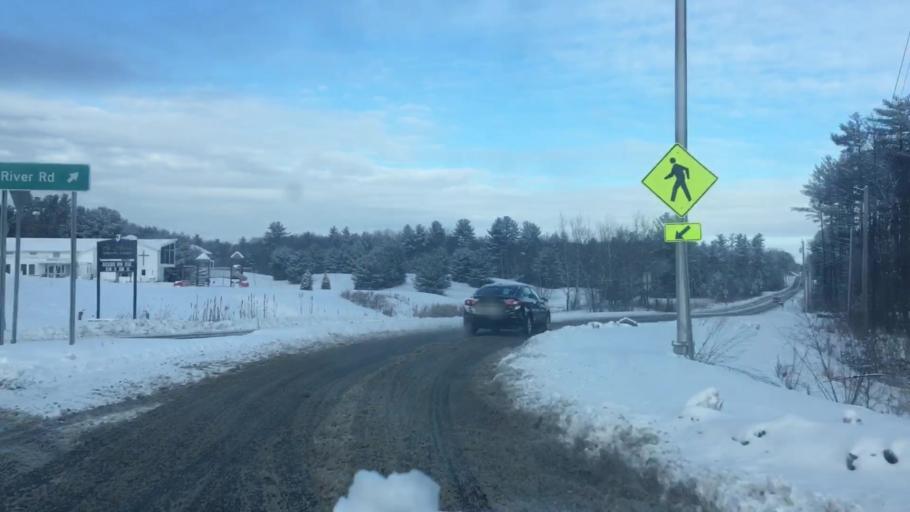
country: US
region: Maine
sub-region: Cumberland County
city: North Windham
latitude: 43.7993
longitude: -70.4401
